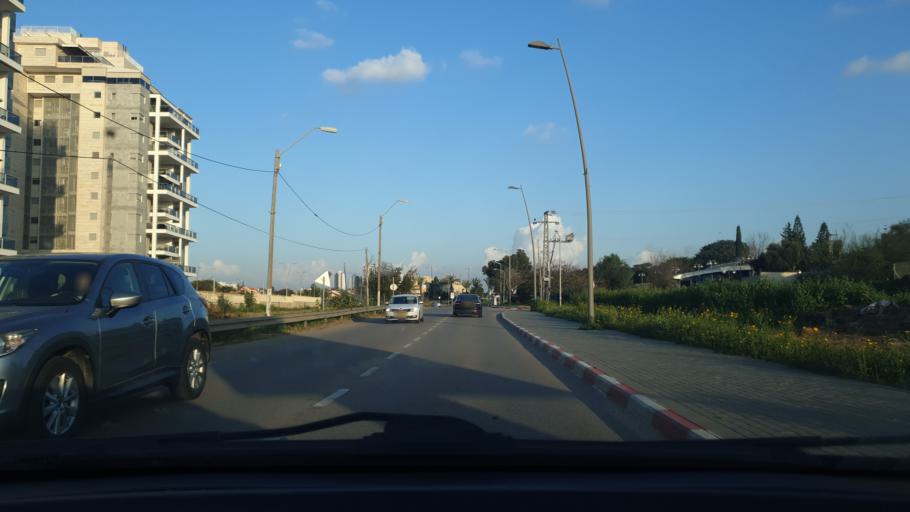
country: IL
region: Central District
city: Ness Ziona
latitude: 31.9333
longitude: 34.8276
